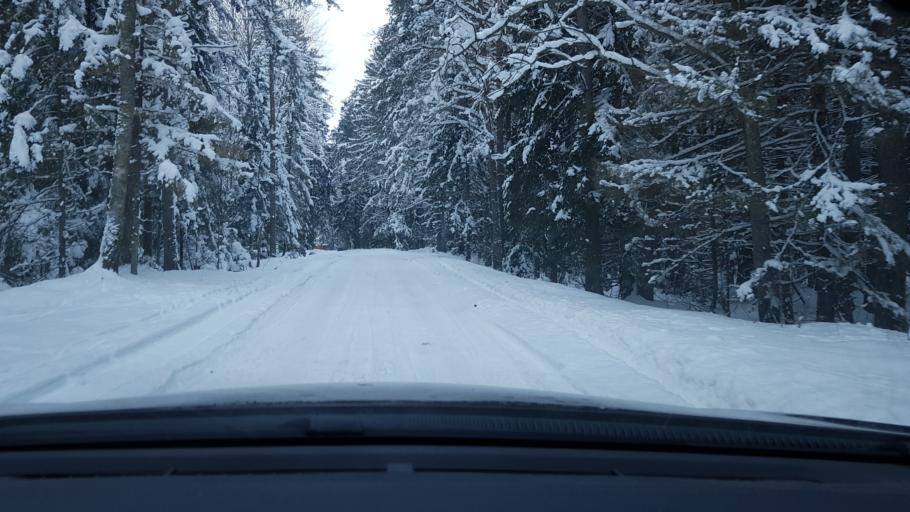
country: EE
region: Harju
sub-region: Harku vald
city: Tabasalu
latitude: 59.4087
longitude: 24.4760
